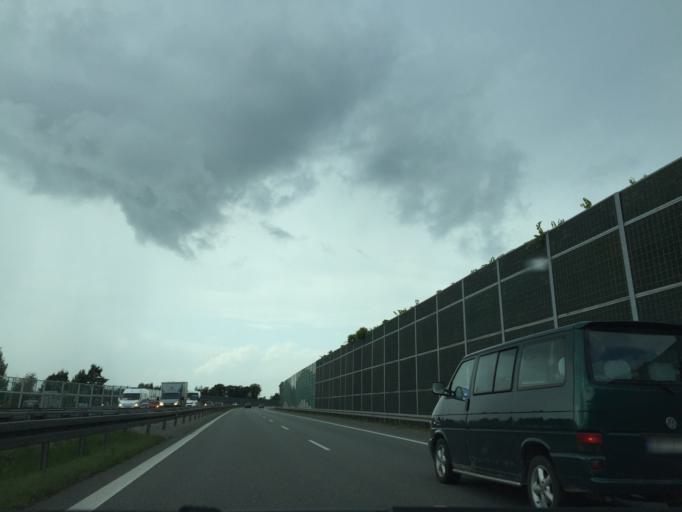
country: PL
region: Masovian Voivodeship
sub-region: Powiat bialobrzeski
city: Stara Blotnica
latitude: 51.5772
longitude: 21.0075
